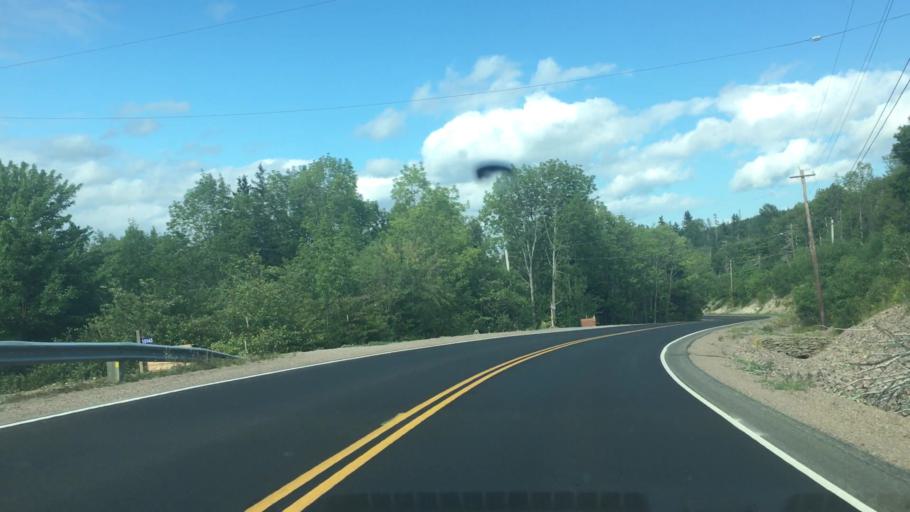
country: CA
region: Nova Scotia
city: Princeville
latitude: 45.7911
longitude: -60.7396
